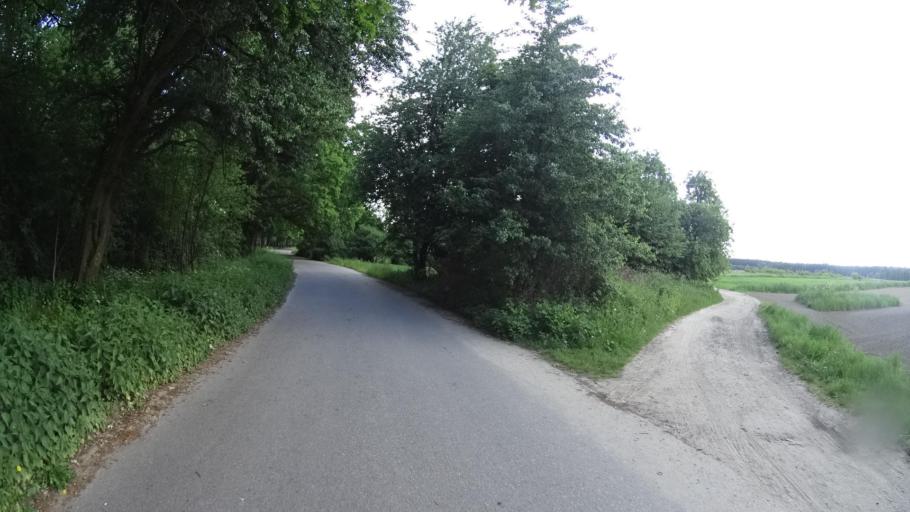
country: PL
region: Masovian Voivodeship
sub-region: Warszawa
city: Kabaty
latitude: 52.1151
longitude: 21.0845
